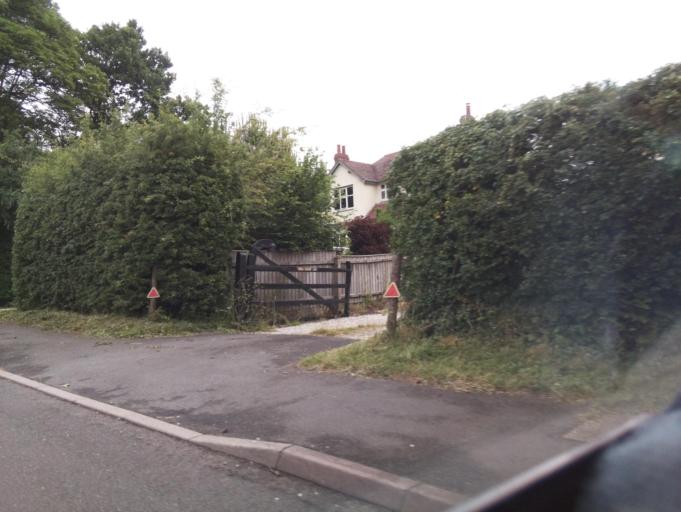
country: GB
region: England
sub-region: Staffordshire
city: Burton upon Trent
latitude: 52.8414
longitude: -1.6698
